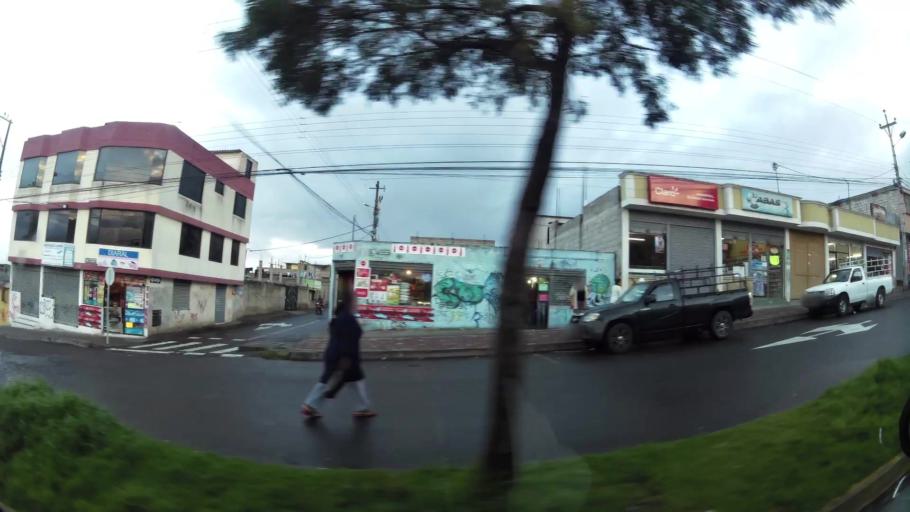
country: EC
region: Pichincha
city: Quito
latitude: -0.0907
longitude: -78.5215
